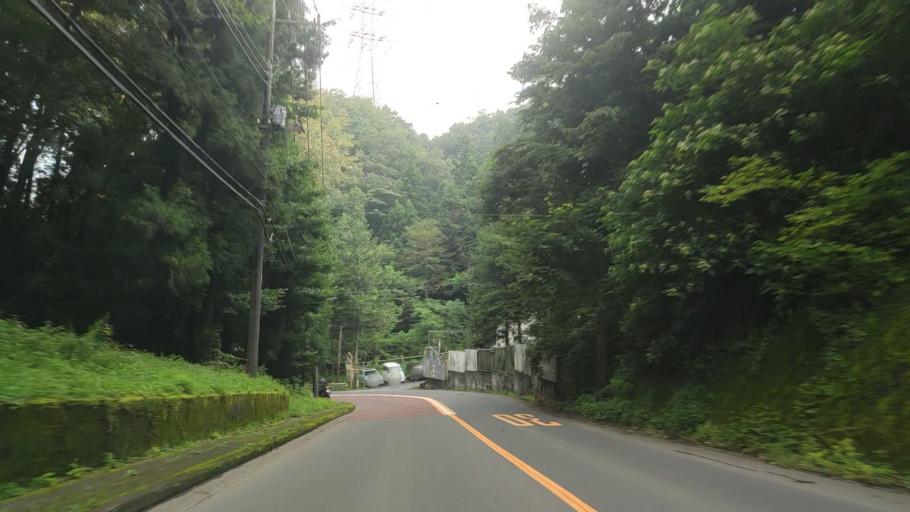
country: JP
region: Saitama
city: Hanno
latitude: 35.8247
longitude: 139.2747
